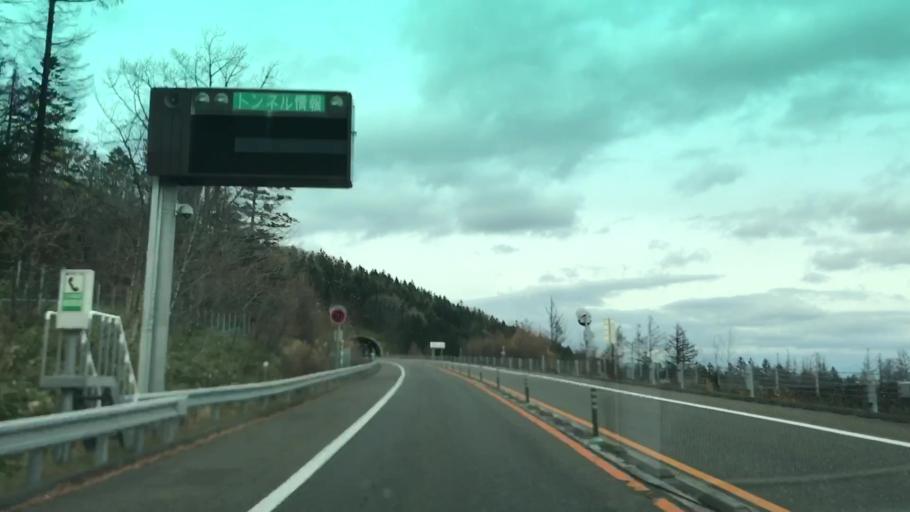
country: JP
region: Hokkaido
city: Otofuke
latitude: 43.0502
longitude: 142.7846
